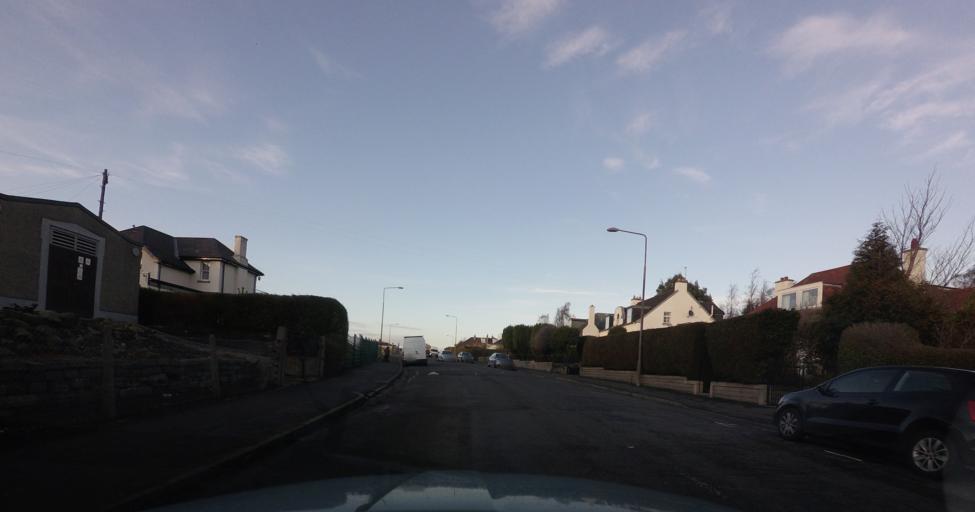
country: GB
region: Scotland
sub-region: Edinburgh
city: Edinburgh
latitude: 55.9687
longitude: -3.2151
